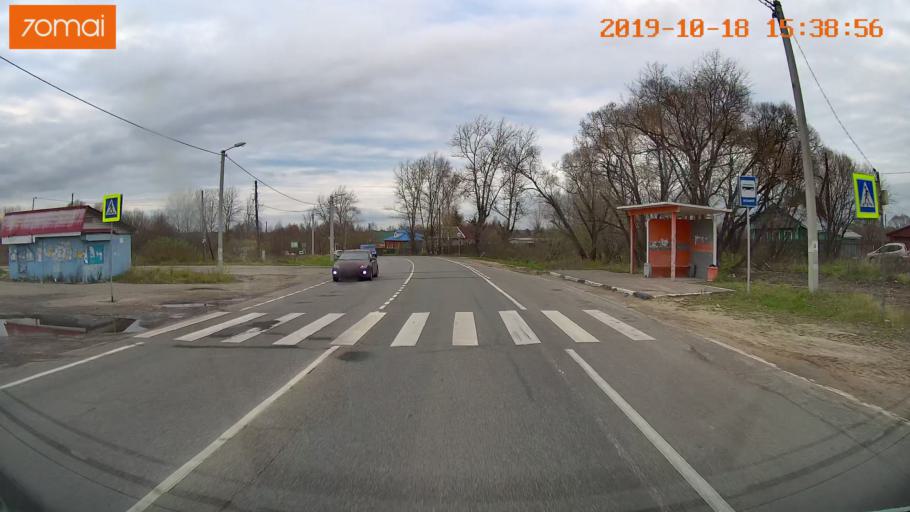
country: RU
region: Vladimir
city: Golovino
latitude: 55.9170
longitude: 40.6075
